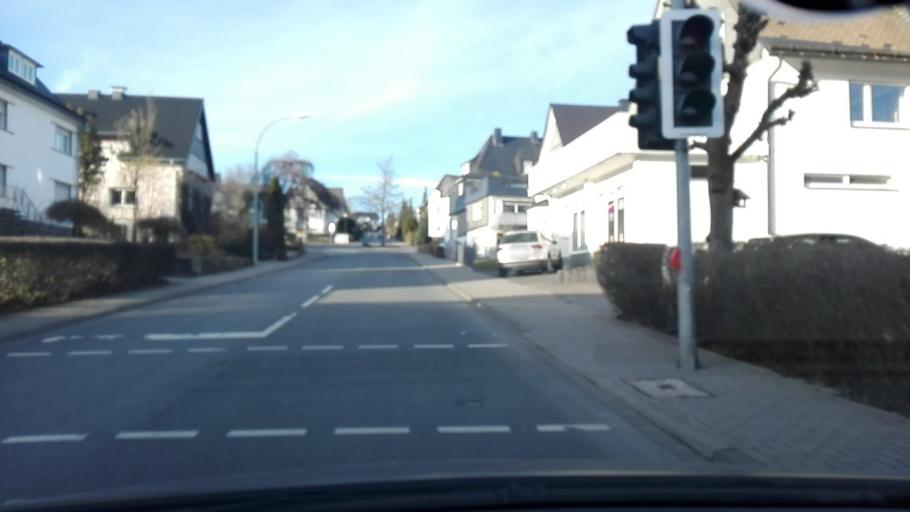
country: DE
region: North Rhine-Westphalia
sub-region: Regierungsbezirk Arnsberg
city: Schmallenberg
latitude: 51.1542
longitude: 8.2833
